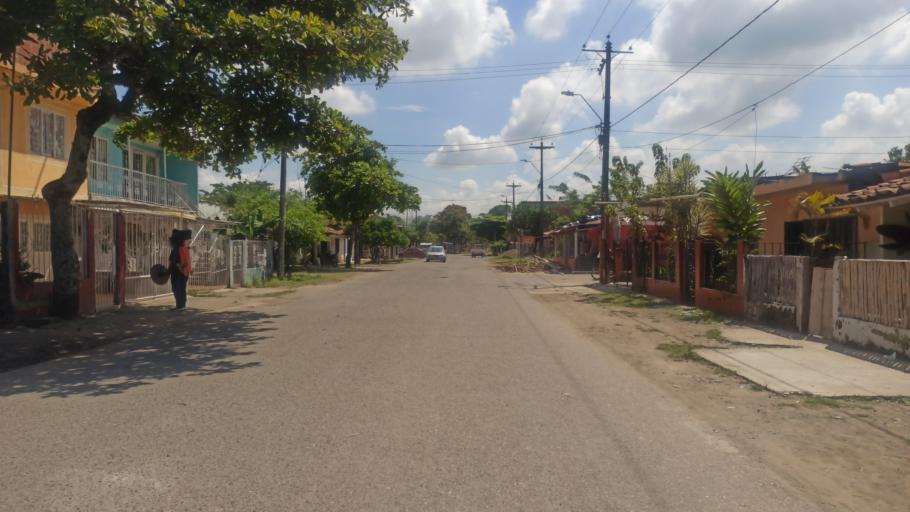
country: CO
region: Valle del Cauca
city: Jamundi
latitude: 3.1340
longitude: -76.5447
